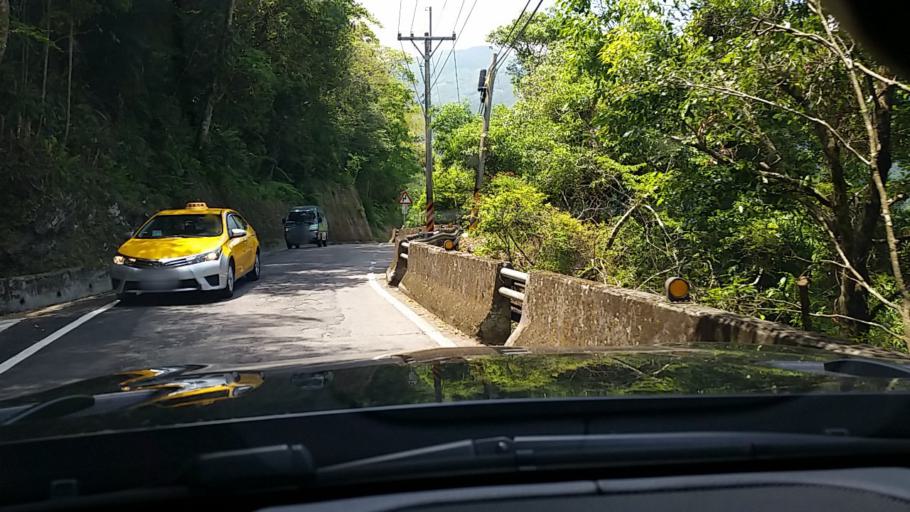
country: TW
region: Taiwan
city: Daxi
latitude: 24.6989
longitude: 121.3730
